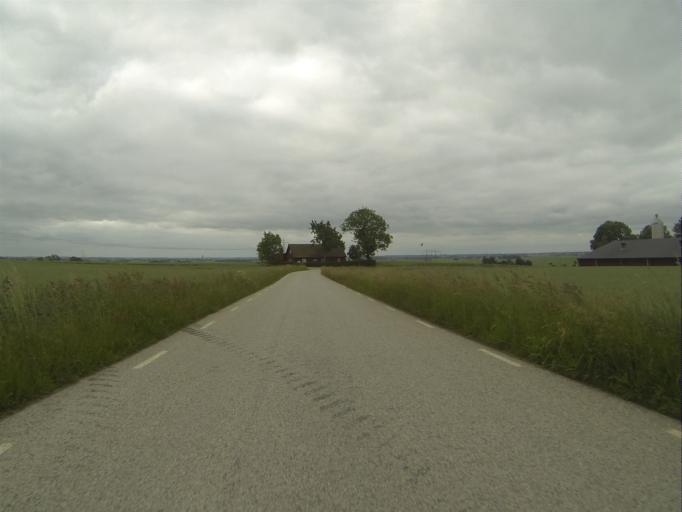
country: SE
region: Skane
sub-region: Staffanstorps Kommun
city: Staffanstorp
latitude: 55.6851
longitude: 13.2870
